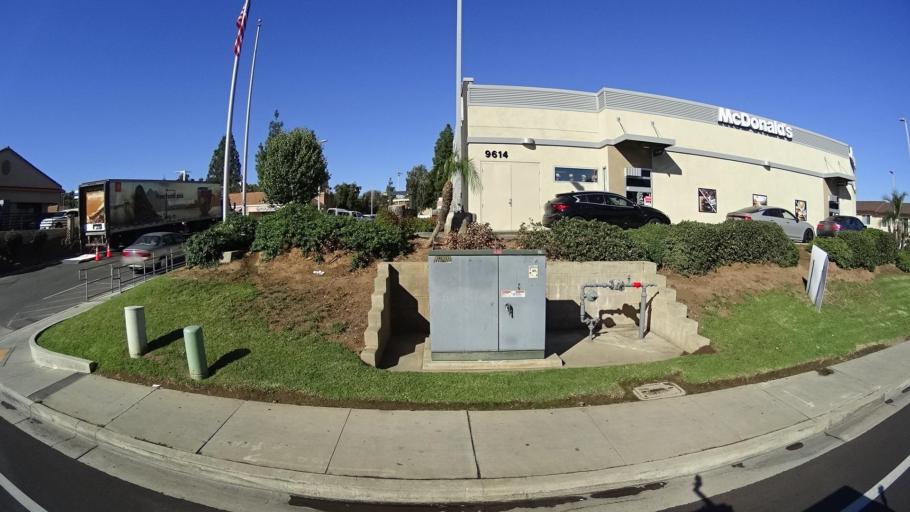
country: US
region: California
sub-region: San Diego County
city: Lakeside
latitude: 32.8528
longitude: -116.9312
